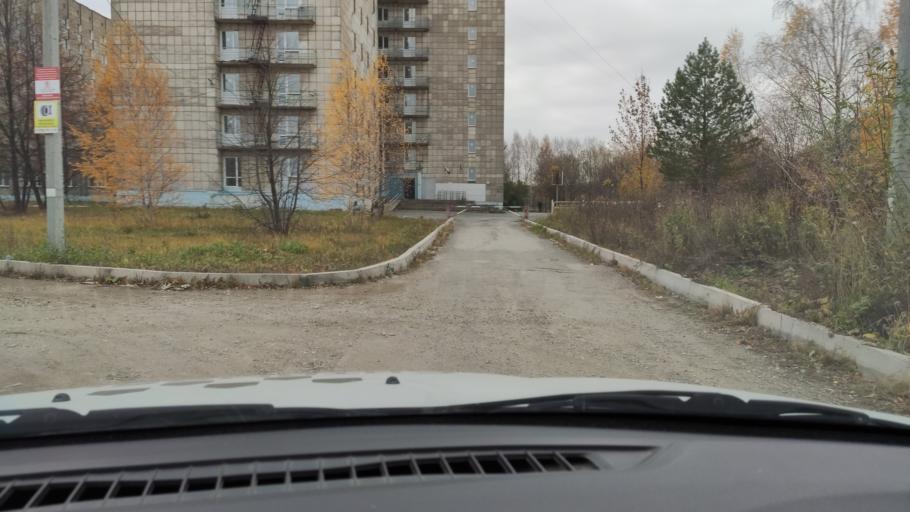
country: RU
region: Perm
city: Froly
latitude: 57.9557
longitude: 56.2738
